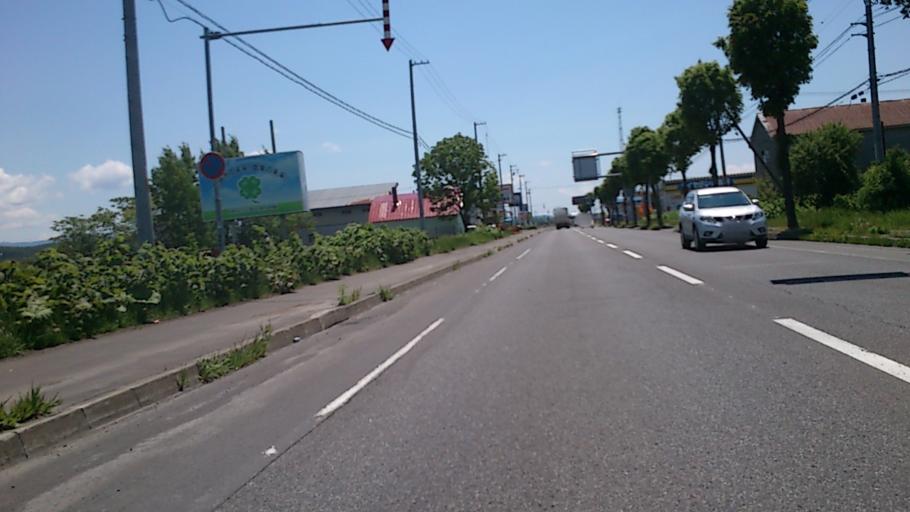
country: JP
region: Hokkaido
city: Nayoro
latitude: 44.3253
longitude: 142.4575
